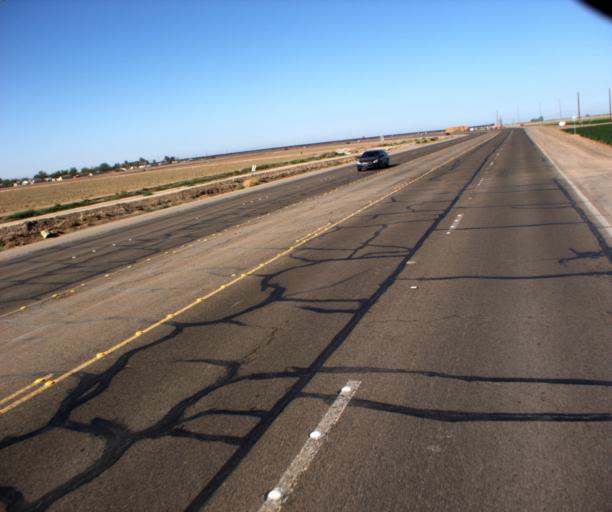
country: US
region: Arizona
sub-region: Yuma County
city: Somerton
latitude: 32.5675
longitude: -114.7780
